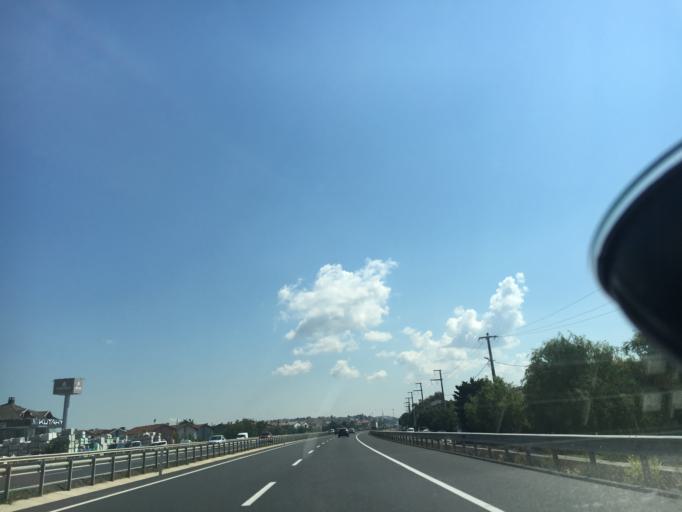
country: TR
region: Istanbul
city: Canta
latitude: 41.0554
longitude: 28.0674
